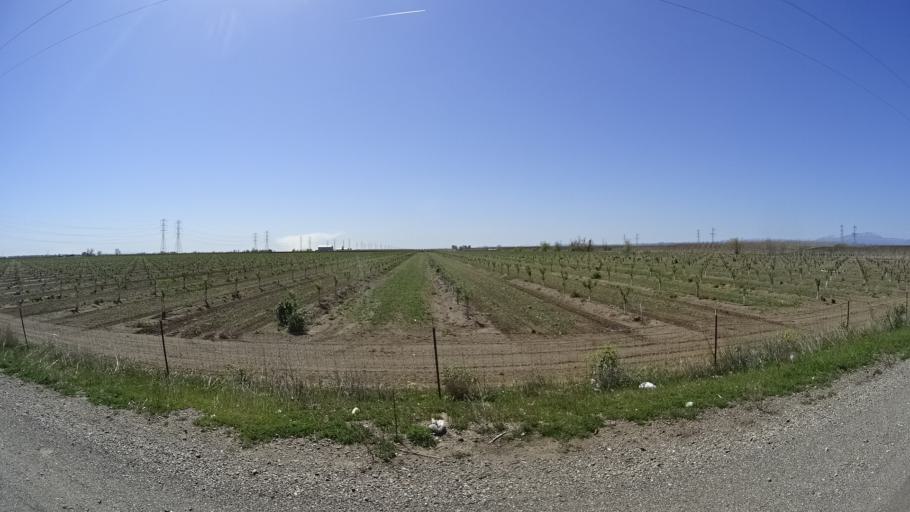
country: US
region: California
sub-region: Glenn County
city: Willows
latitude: 39.6248
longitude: -122.2671
